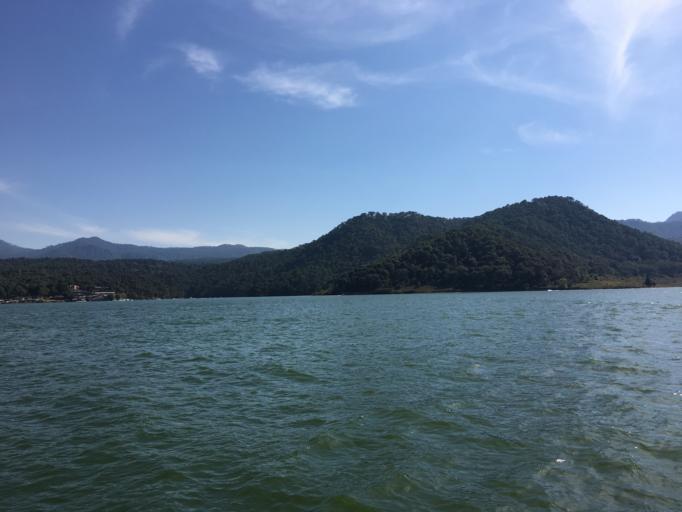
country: MX
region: Mexico
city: Valle de Bravo
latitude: 19.1875
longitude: -100.1495
